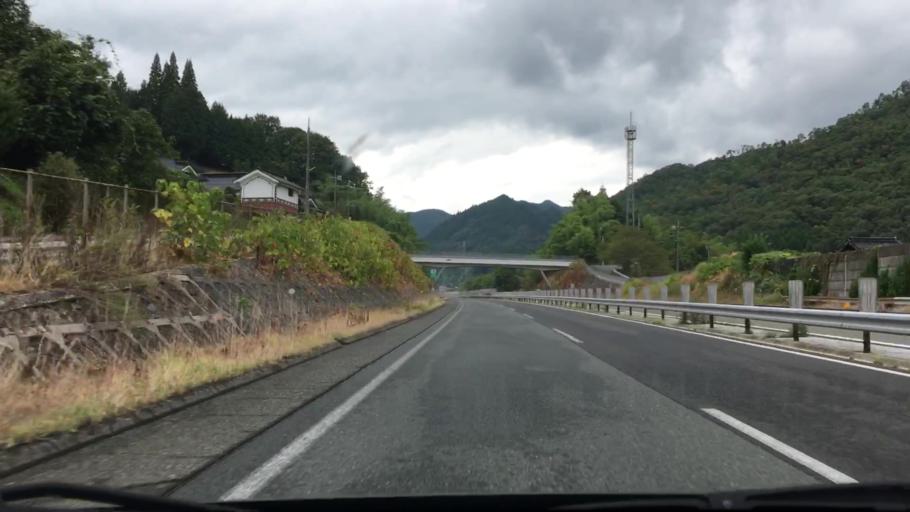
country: JP
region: Okayama
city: Niimi
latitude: 35.0030
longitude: 133.4422
